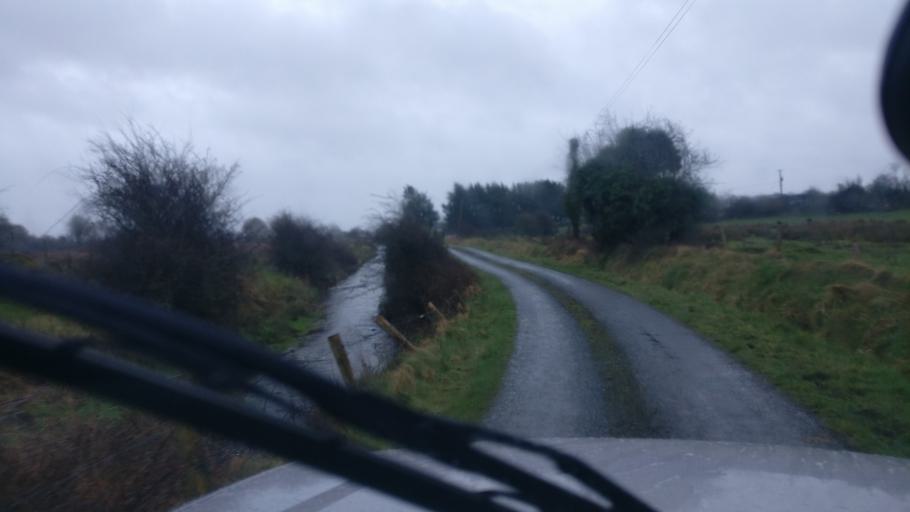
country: IE
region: Connaught
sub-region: County Galway
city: Ballinasloe
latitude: 53.2460
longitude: -8.3458
